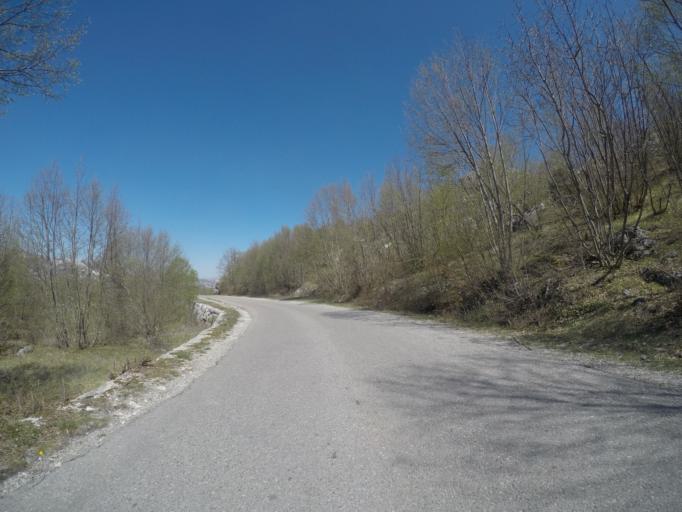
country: ME
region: Cetinje
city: Cetinje
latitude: 42.4466
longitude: 18.8735
